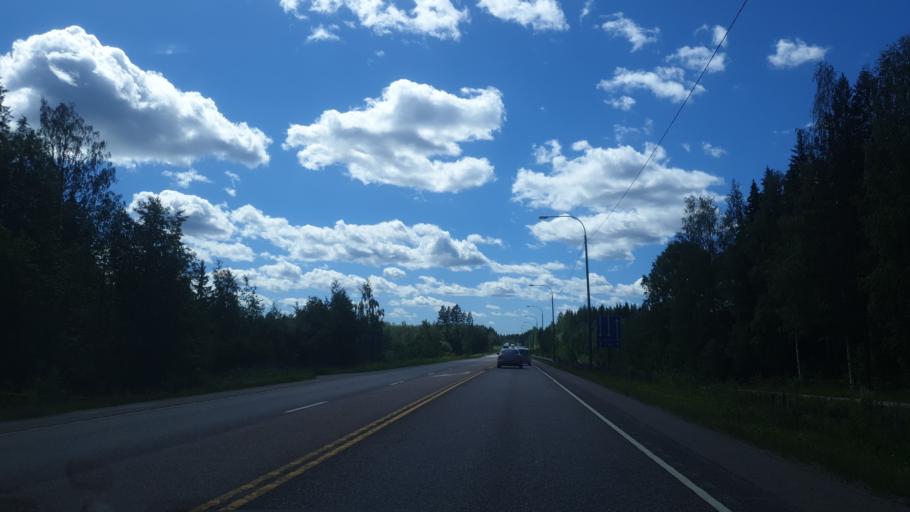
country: FI
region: Northern Savo
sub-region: Varkaus
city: Varkaus
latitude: 62.3957
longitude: 27.8190
